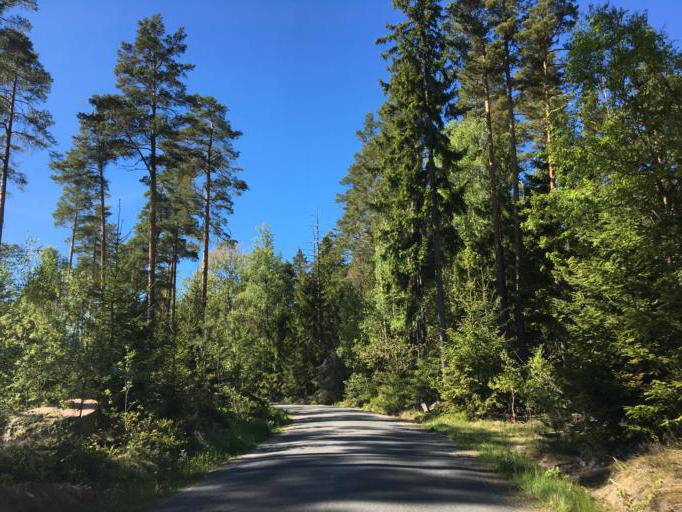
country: SE
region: Soedermanland
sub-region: Eskilstuna Kommun
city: Hallbybrunn
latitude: 59.3517
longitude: 16.3918
